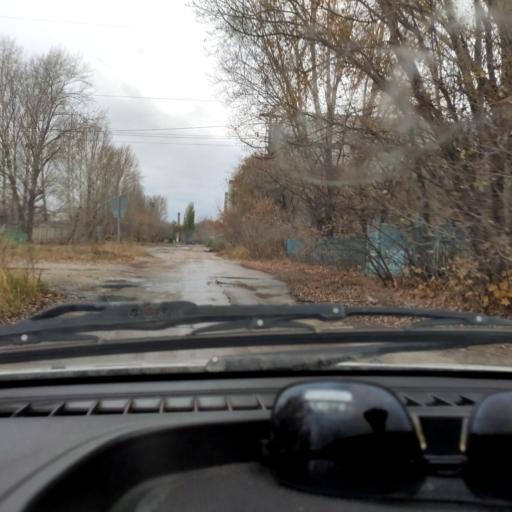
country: RU
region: Samara
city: Tol'yatti
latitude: 53.5171
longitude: 49.4625
